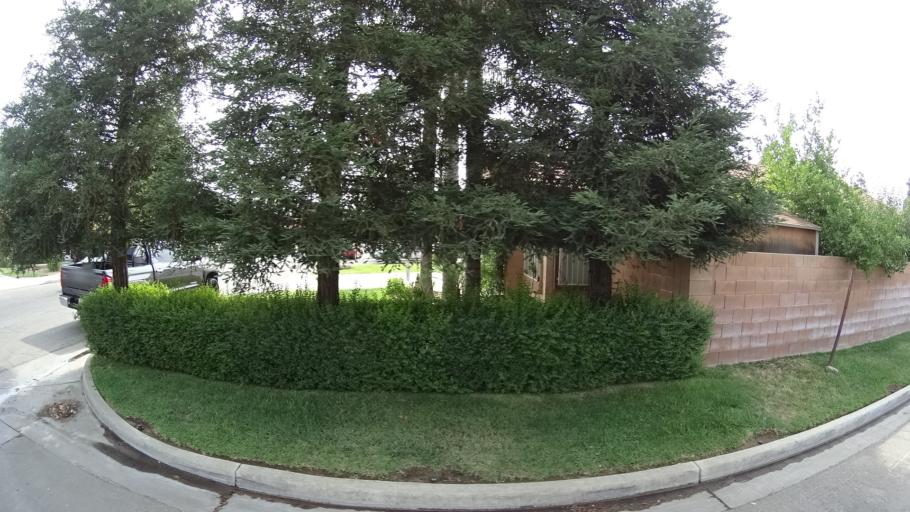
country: US
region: California
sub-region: Fresno County
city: West Park
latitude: 36.7698
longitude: -119.8706
